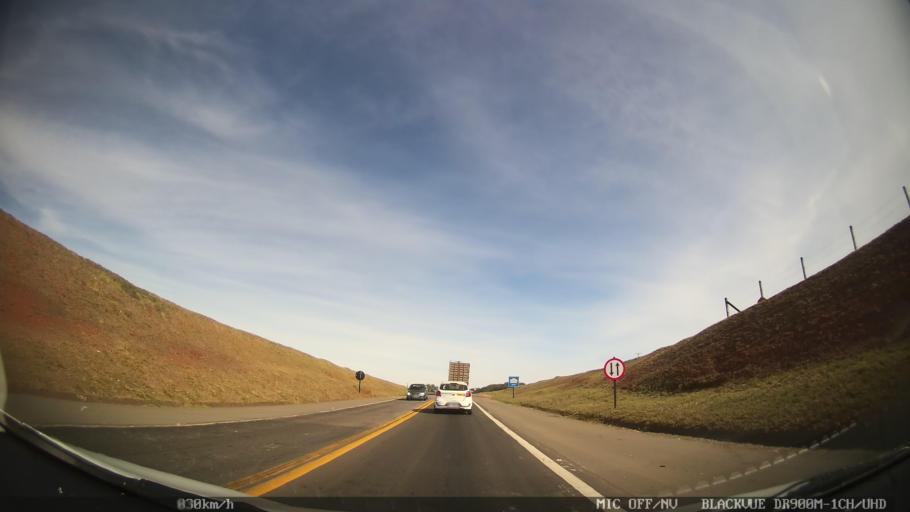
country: BR
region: Sao Paulo
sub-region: Rio Das Pedras
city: Rio das Pedras
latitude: -22.7942
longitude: -47.5830
